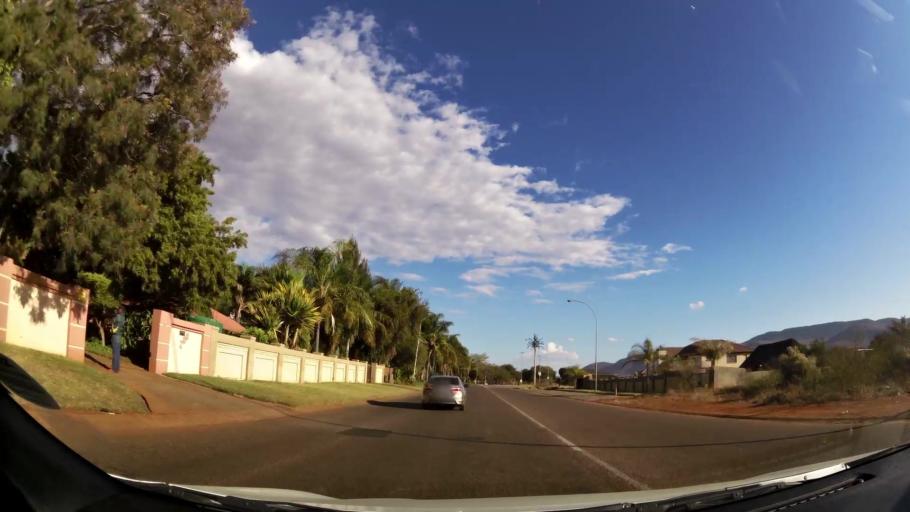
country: ZA
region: Limpopo
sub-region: Waterberg District Municipality
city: Mokopane
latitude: -24.2021
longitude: 29.0017
